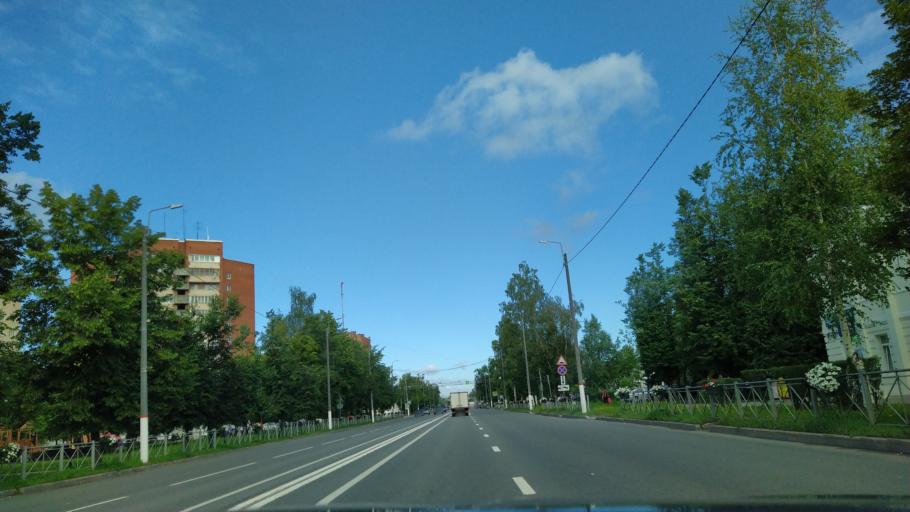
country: RU
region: Leningrad
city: Tosno
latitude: 59.5381
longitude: 30.8823
